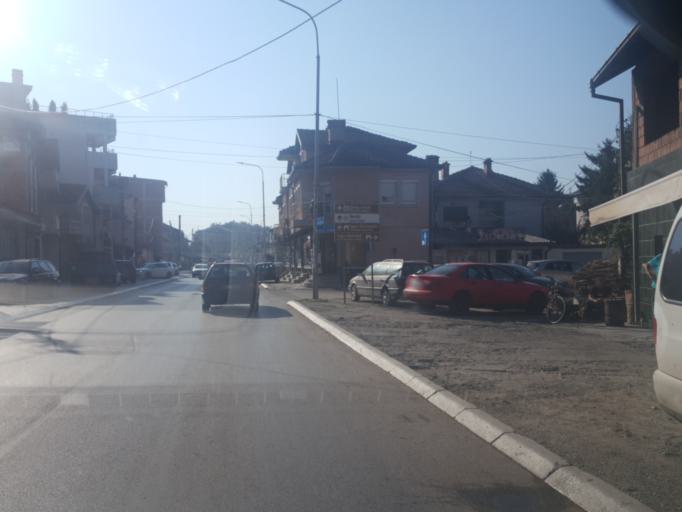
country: XK
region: Gjakova
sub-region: Komuna e Gjakoves
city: Gjakove
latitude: 42.3908
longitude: 20.4254
